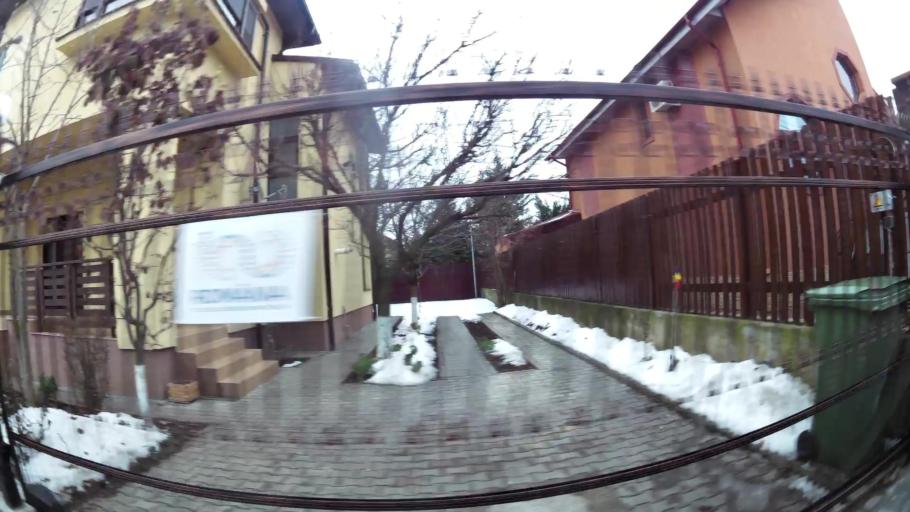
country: RO
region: Ilfov
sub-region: Comuna Otopeni
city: Otopeni
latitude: 44.5564
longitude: 26.0760
